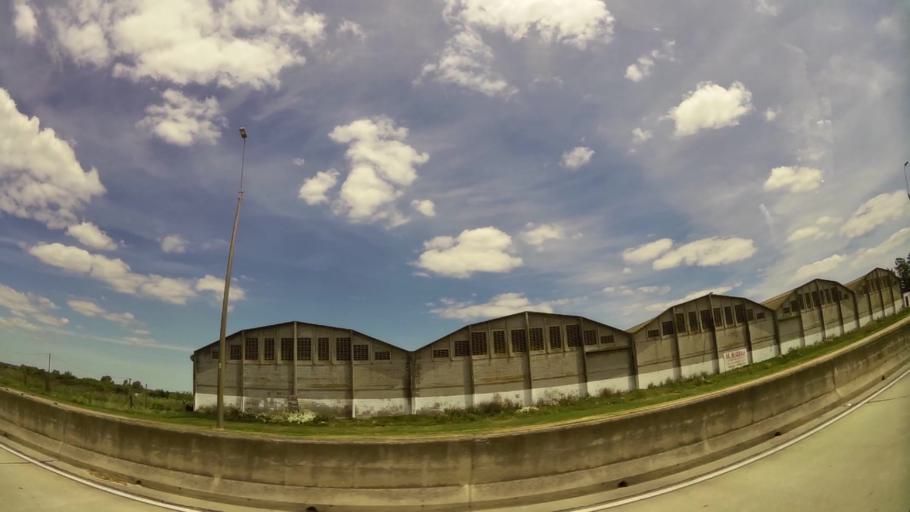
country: UY
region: San Jose
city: Delta del Tigre
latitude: -34.7692
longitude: -56.3893
